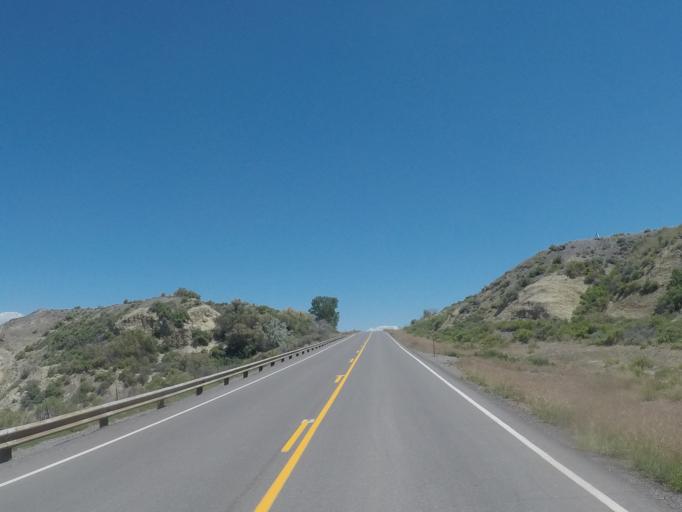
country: US
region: Wyoming
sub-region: Big Horn County
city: Lovell
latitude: 44.7769
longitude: -108.4981
